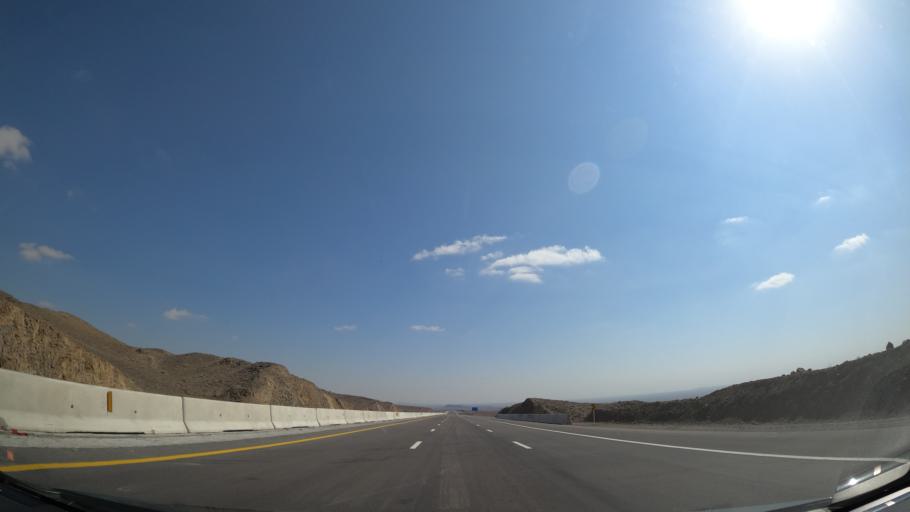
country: IR
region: Alborz
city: Nazarabad
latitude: 35.6569
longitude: 50.6634
